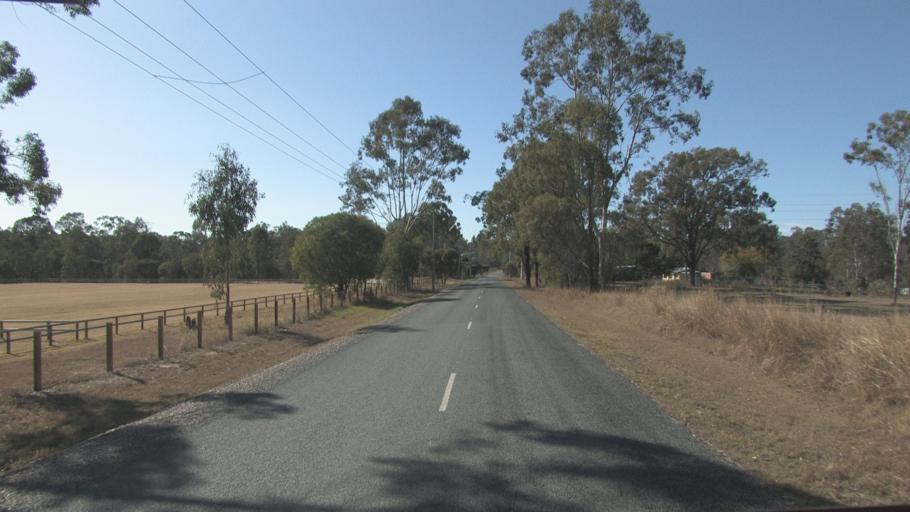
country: AU
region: Queensland
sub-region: Logan
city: Cedar Vale
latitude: -27.8410
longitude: 153.0285
